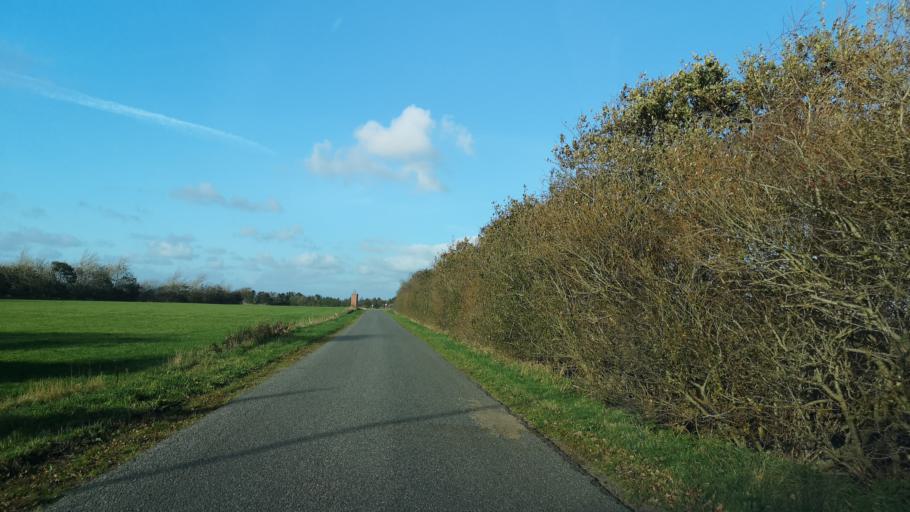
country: DK
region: Central Jutland
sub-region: Ringkobing-Skjern Kommune
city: Skjern
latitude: 55.8542
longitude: 8.3502
